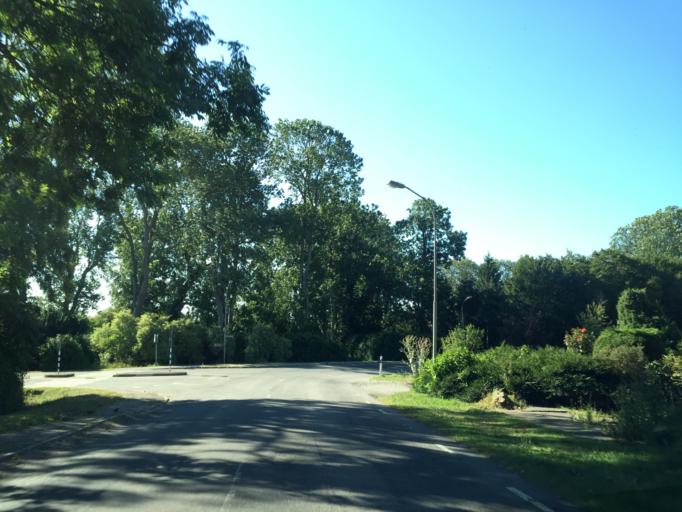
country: SE
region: Skane
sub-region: Ystads Kommun
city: Kopingebro
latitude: 55.4440
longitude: 14.1217
